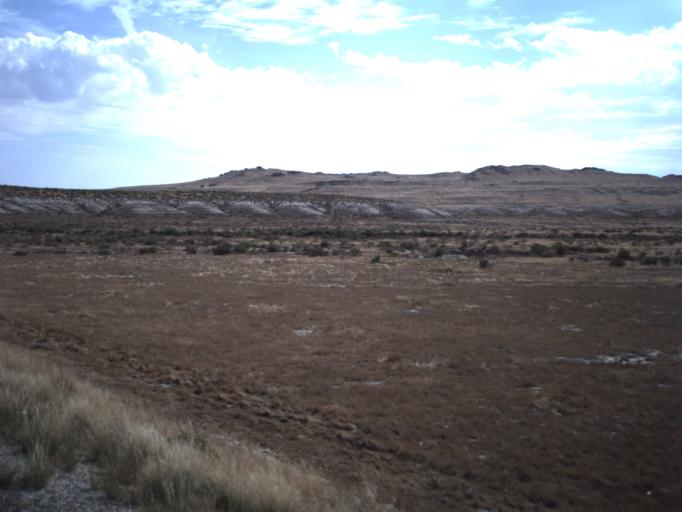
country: US
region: Utah
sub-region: Tooele County
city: Wendover
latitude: 41.4062
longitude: -113.9386
